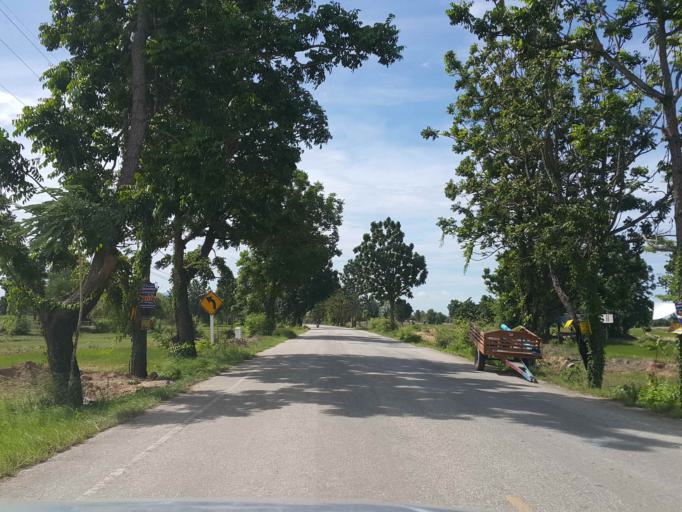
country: TH
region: Sukhothai
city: Ban Dan Lan Hoi
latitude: 17.1390
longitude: 99.5243
